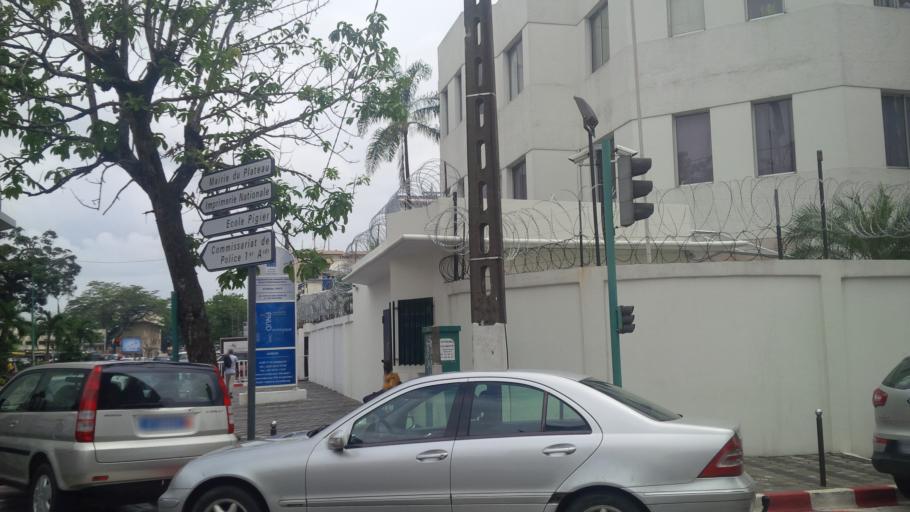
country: CI
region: Lagunes
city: Abidjan
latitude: 5.3253
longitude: -4.0186
